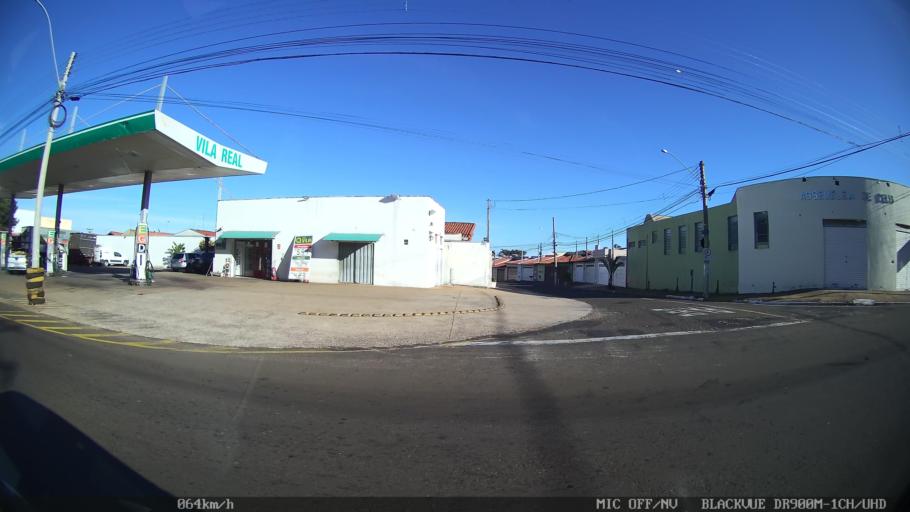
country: BR
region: Sao Paulo
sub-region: Franca
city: Franca
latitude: -20.5681
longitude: -47.3661
